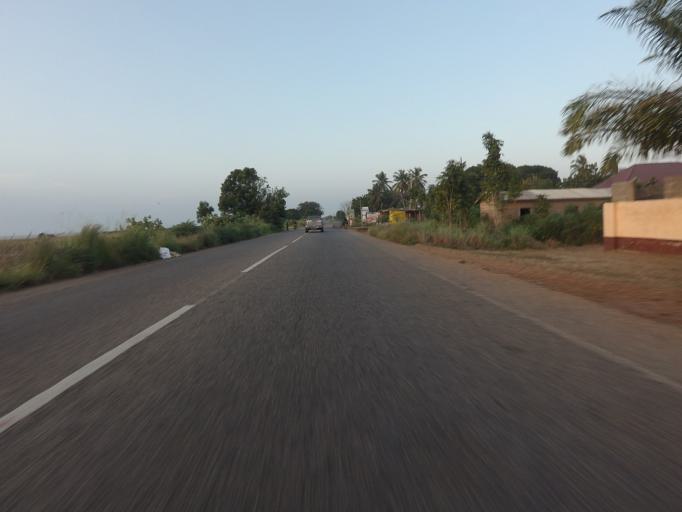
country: GH
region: Volta
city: Anloga
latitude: 5.8154
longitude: 0.9390
